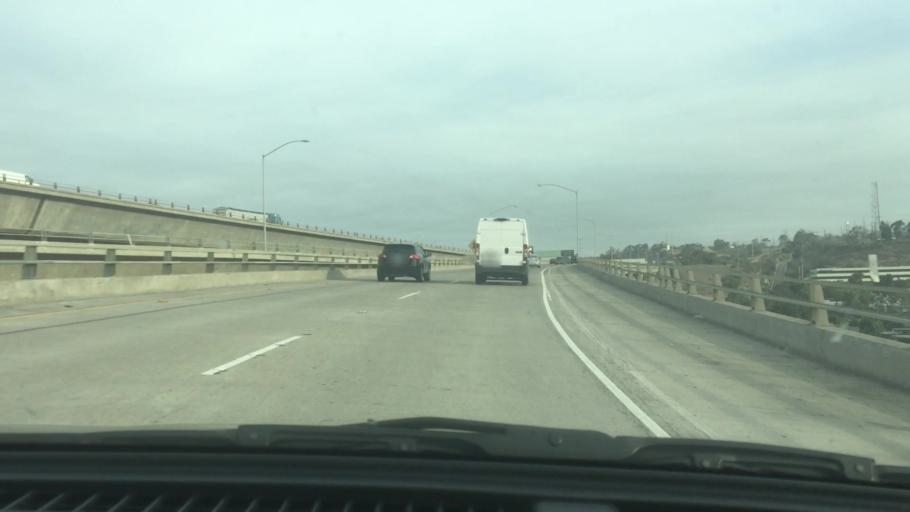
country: US
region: California
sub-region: San Diego County
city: San Diego
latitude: 32.7730
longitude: -117.1333
